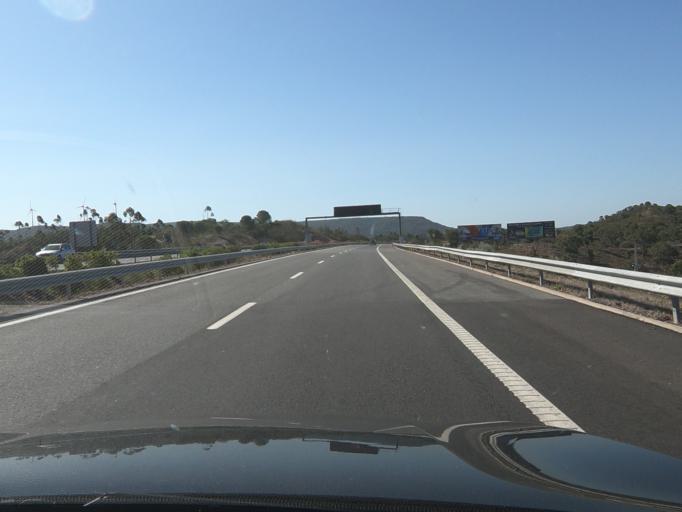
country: PT
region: Faro
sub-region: Silves
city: Sao Bartolomeu de Messines
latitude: 37.2779
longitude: -8.2632
